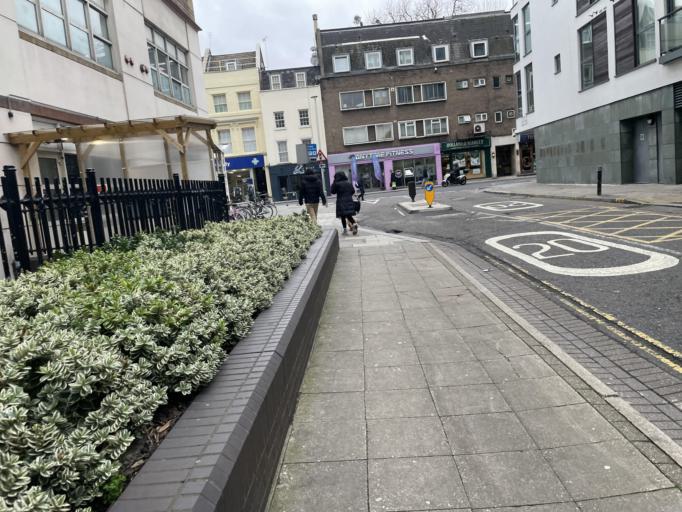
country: GB
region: England
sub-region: Greater London
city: Chelsea
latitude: 51.4850
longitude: -0.1816
